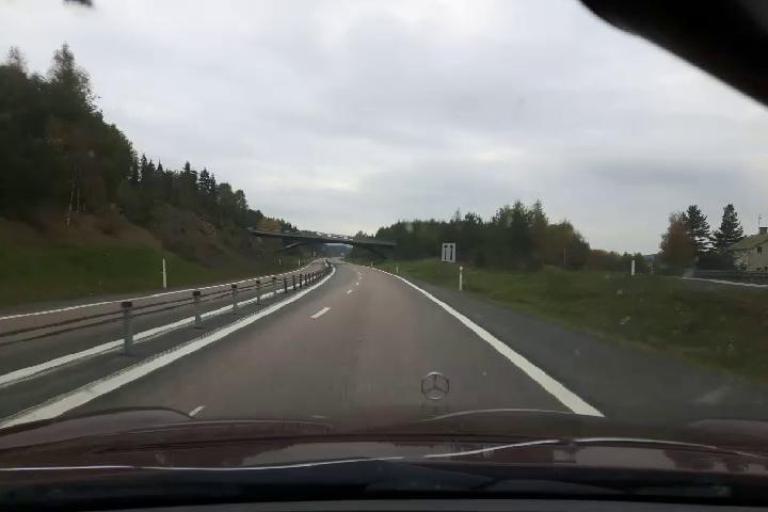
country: SE
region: Vaesternorrland
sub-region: Kramfors Kommun
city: Nordingra
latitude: 62.9313
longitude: 18.0960
